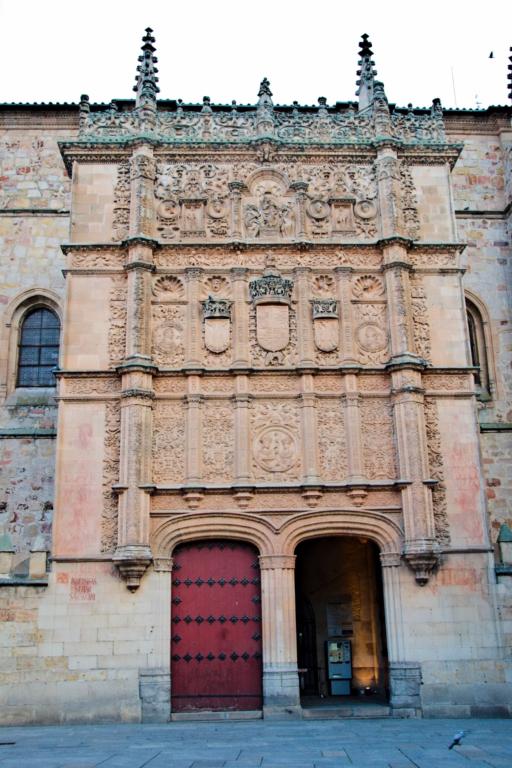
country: ES
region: Castille and Leon
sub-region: Provincia de Salamanca
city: Salamanca
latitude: 40.9615
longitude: -5.6675
